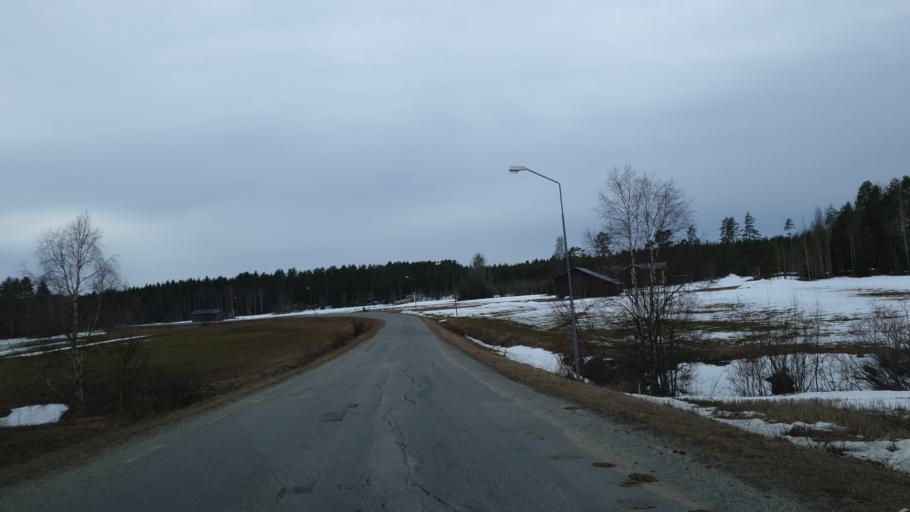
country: SE
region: Vaesterbotten
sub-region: Robertsfors Kommun
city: Robertsfors
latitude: 64.4009
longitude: 21.0058
